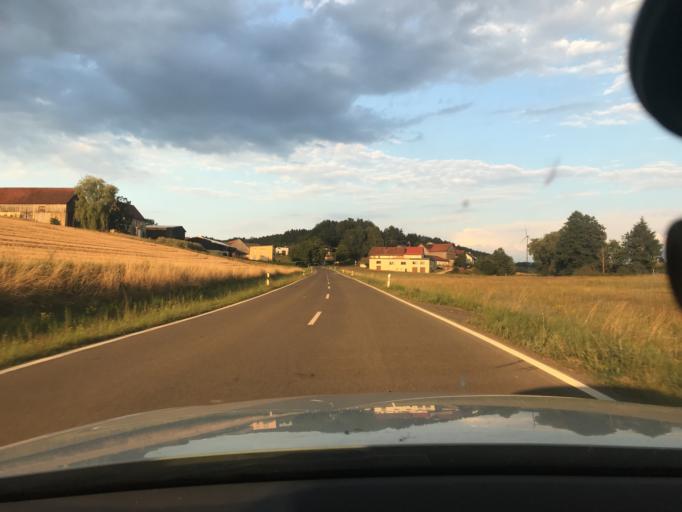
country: DE
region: Bavaria
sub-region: Upper Palatinate
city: Auerbach
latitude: 49.7473
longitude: 11.6156
